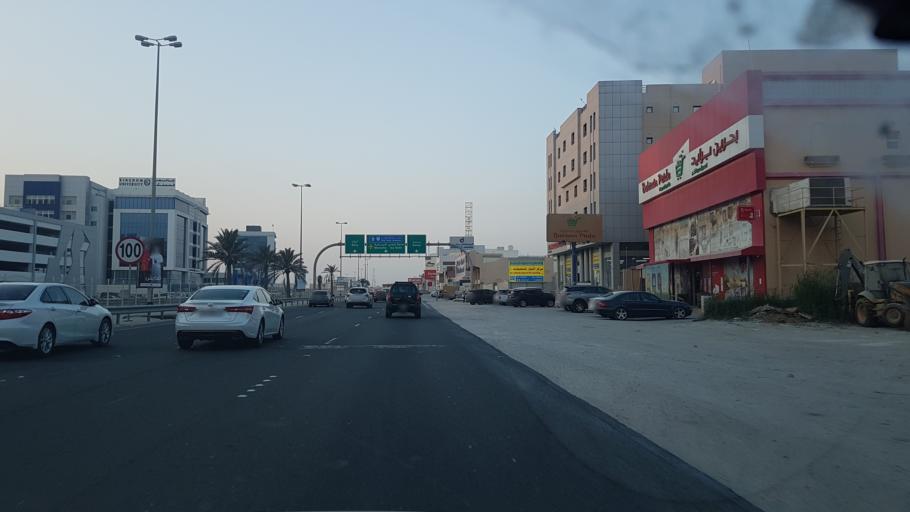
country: BH
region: Northern
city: Ar Rifa'
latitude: 26.1346
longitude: 50.5849
